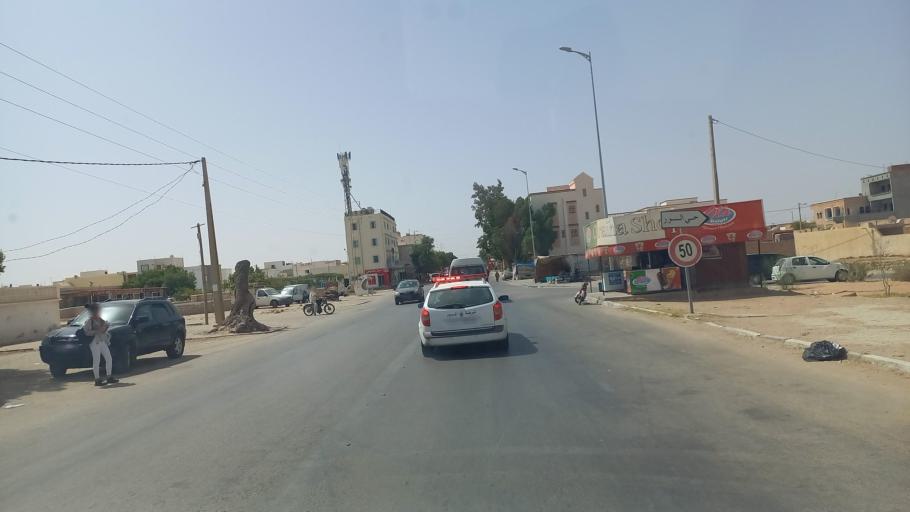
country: TN
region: Madanin
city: Medenine
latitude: 33.3298
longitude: 10.4851
